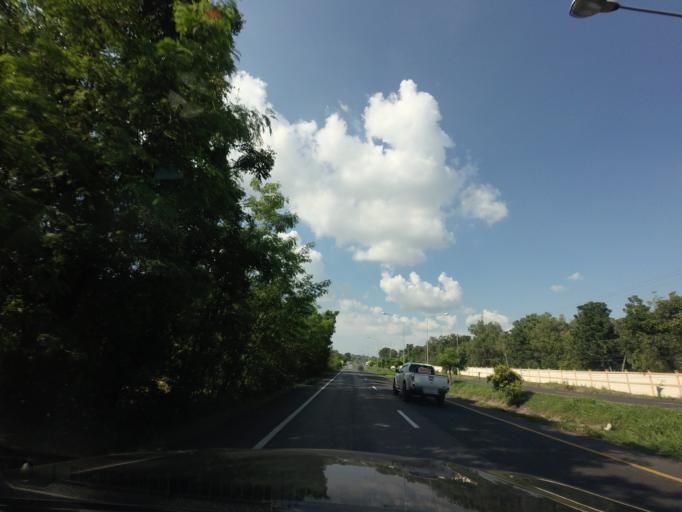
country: TH
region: Nakhon Ratchasima
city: Bua Lai
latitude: 15.6773
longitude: 102.5763
